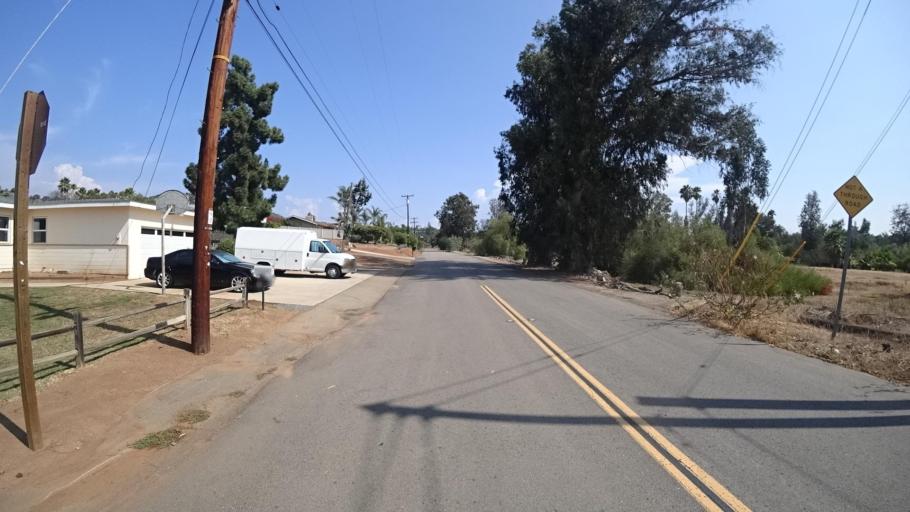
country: US
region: California
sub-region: San Diego County
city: Escondido
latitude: 33.1185
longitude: -117.0427
